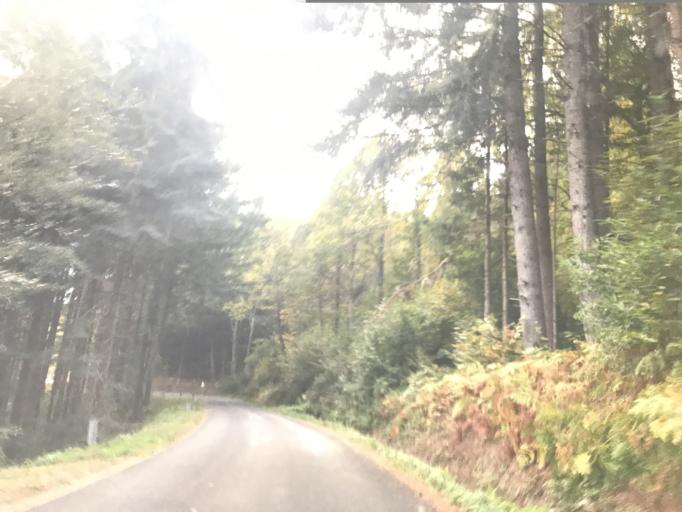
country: FR
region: Auvergne
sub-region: Departement du Puy-de-Dome
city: Celles-sur-Durolle
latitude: 45.7852
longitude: 3.6422
